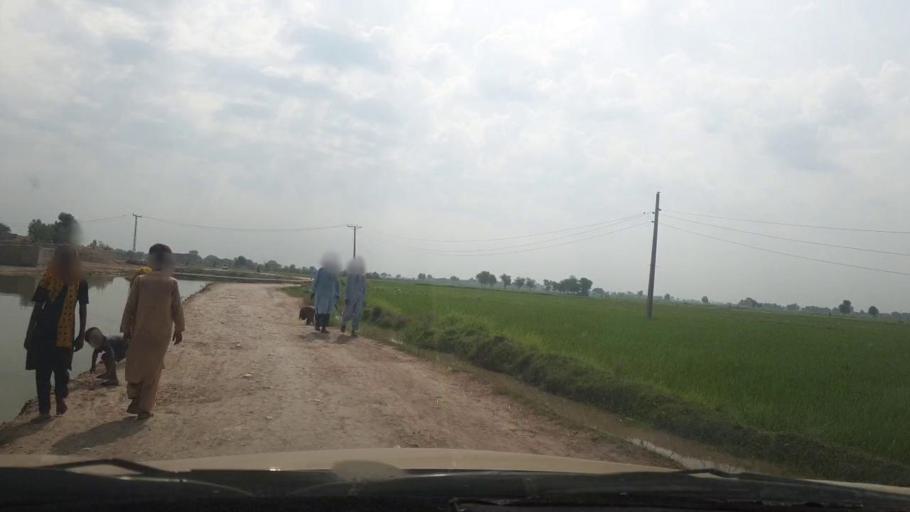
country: PK
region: Sindh
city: Larkana
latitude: 27.6516
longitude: 68.1986
